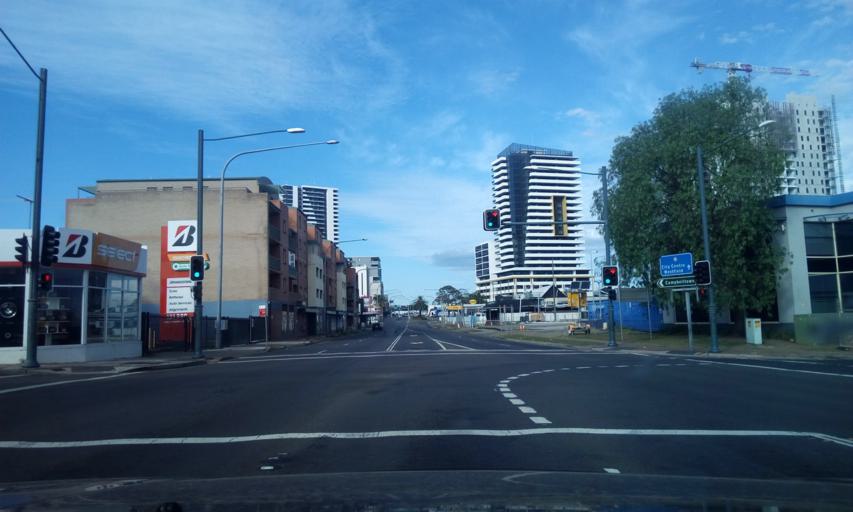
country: AU
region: New South Wales
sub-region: Fairfield
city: Liverpool
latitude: -33.9261
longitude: 150.9230
